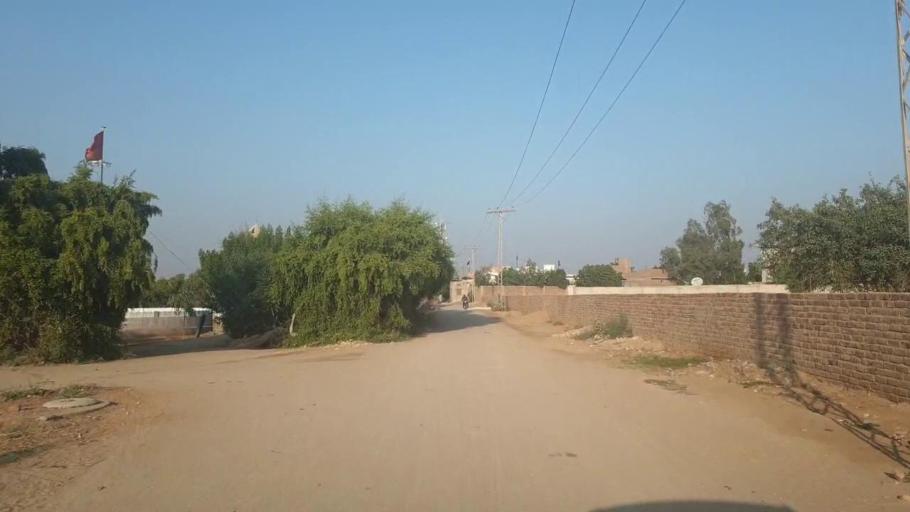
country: PK
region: Sindh
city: Jamshoro
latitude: 25.4411
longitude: 68.2917
